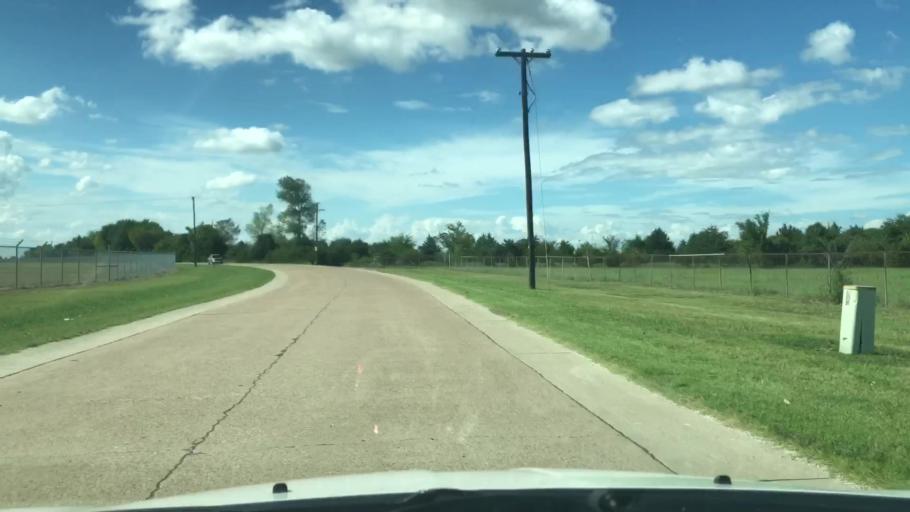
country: US
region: Texas
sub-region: Navarro County
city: Corsicana
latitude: 32.0312
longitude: -96.3961
